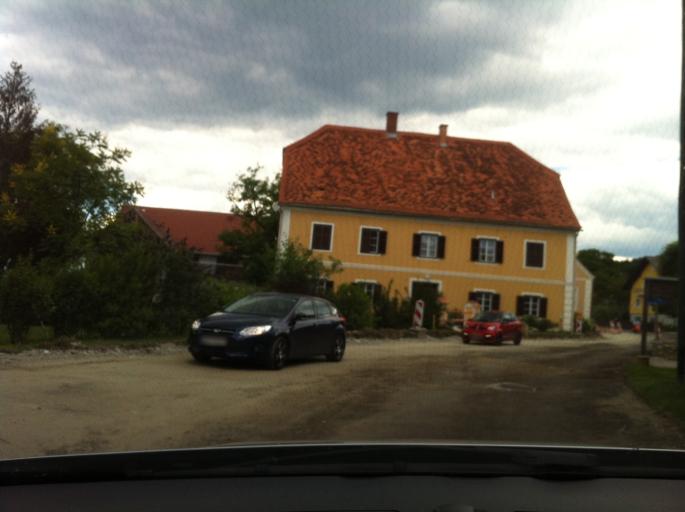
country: AT
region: Styria
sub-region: Politischer Bezirk Hartberg-Fuerstenfeld
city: Ebersdorf
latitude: 47.1999
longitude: 15.9585
